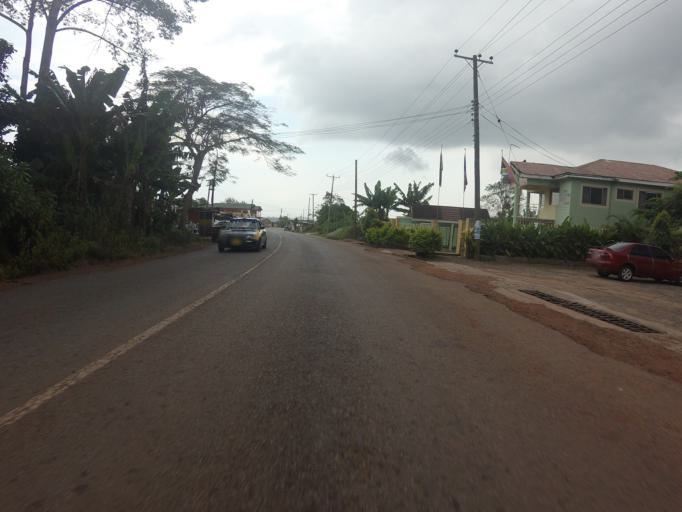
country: GH
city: Akropong
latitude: 5.9417
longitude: -0.1187
